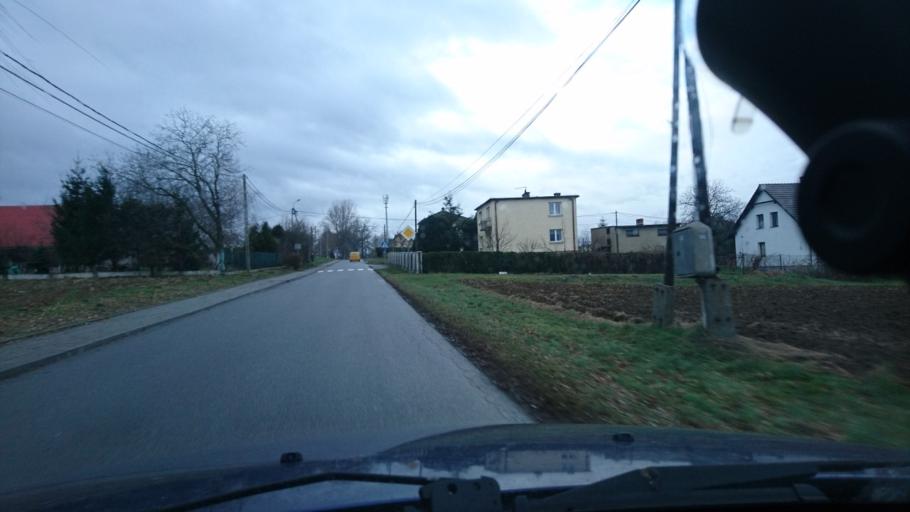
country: PL
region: Silesian Voivodeship
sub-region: Powiat bielski
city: Bestwinka
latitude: 49.9194
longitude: 19.0598
